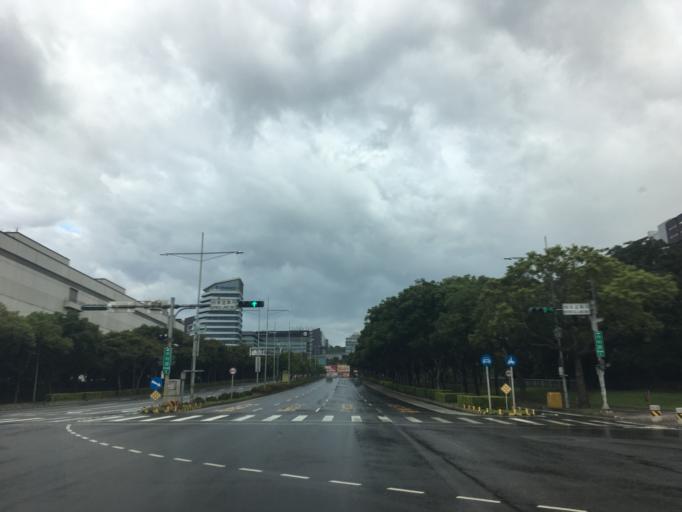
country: TW
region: Taiwan
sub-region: Taichung City
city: Taichung
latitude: 24.2092
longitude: 120.6162
